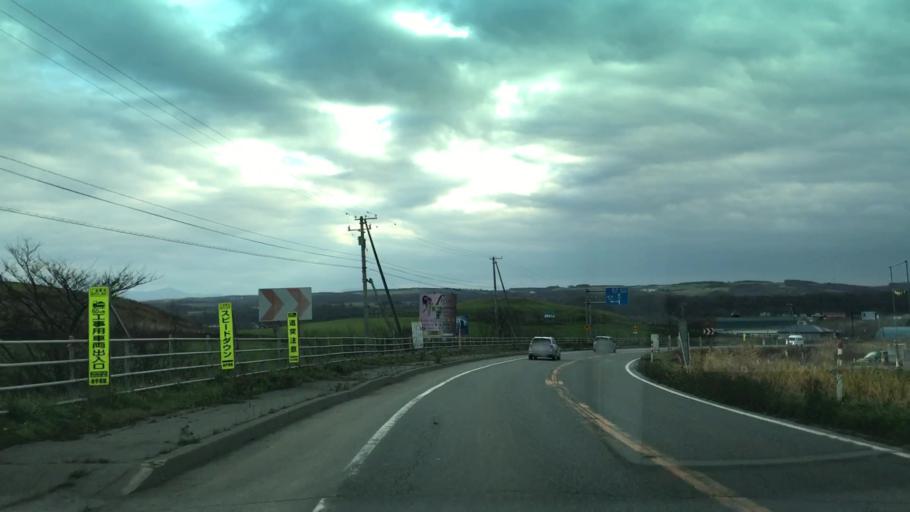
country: JP
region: Hokkaido
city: Shizunai-furukawacho
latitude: 42.3754
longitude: 142.3067
